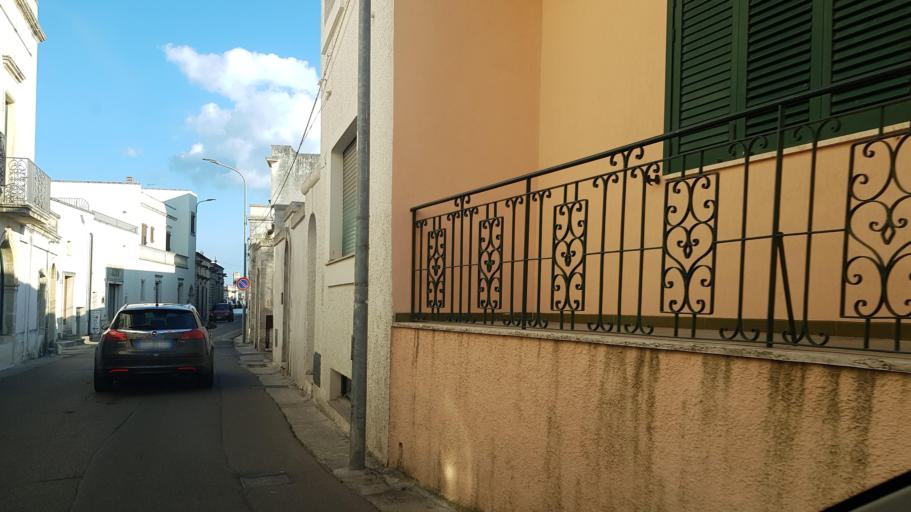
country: IT
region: Apulia
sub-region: Provincia di Lecce
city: Marittima
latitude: 39.9969
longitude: 18.3973
